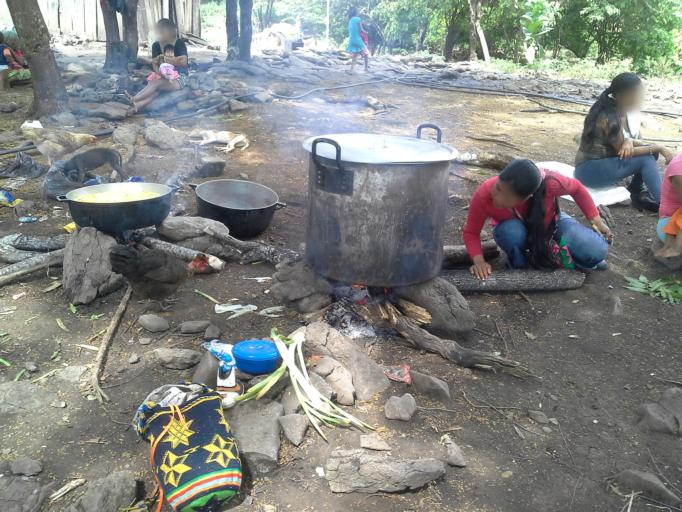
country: CO
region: Cesar
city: Becerril
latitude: 9.7506
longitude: -73.1386
